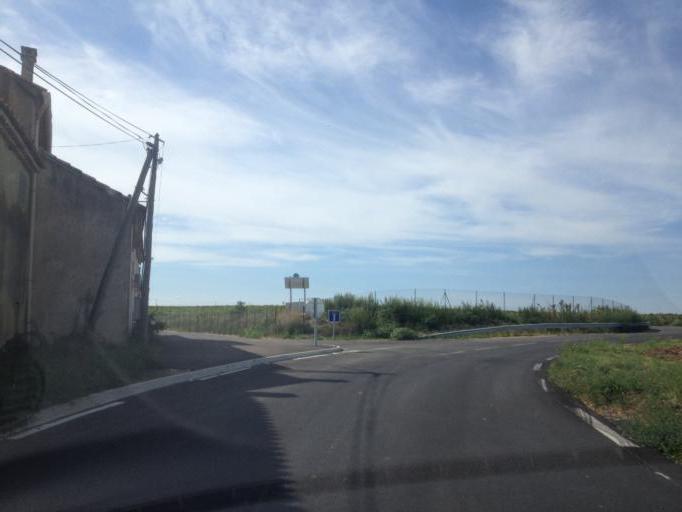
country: FR
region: Provence-Alpes-Cote d'Azur
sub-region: Departement du Vaucluse
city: Courthezon
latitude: 44.0974
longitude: 4.8571
